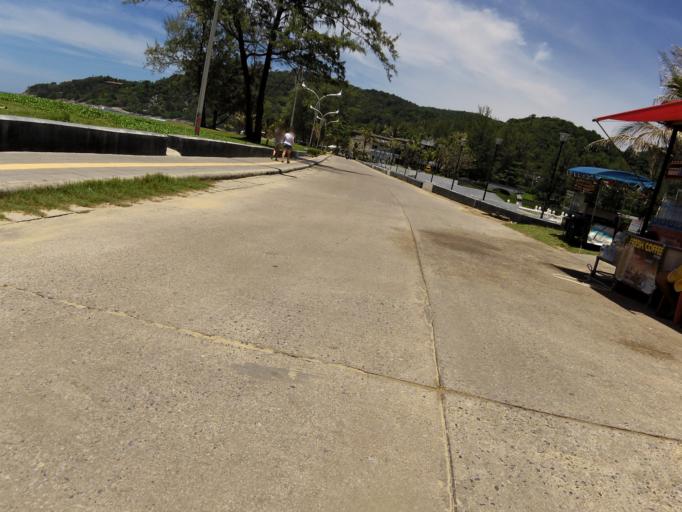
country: TH
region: Phuket
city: Ban Karon
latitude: 7.8516
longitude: 98.2925
